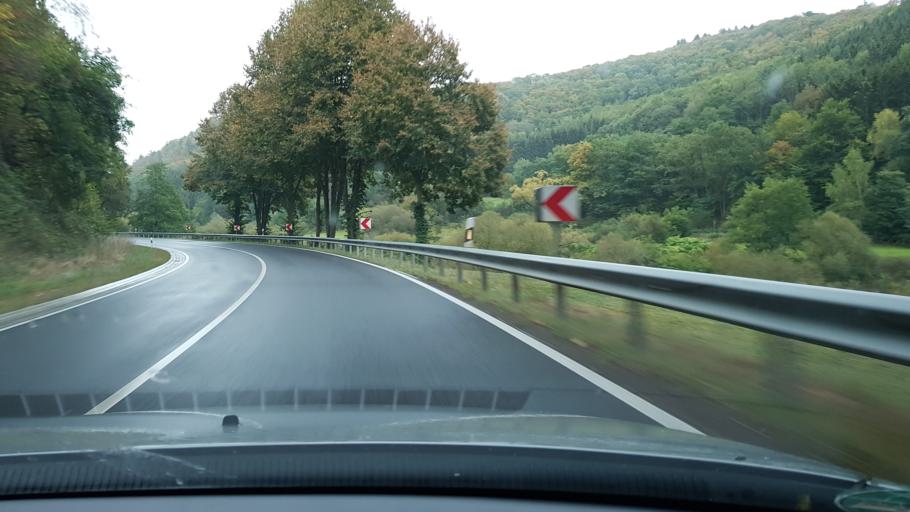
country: DE
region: Rheinland-Pfalz
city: Misselberg
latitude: 50.3150
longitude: 7.7701
